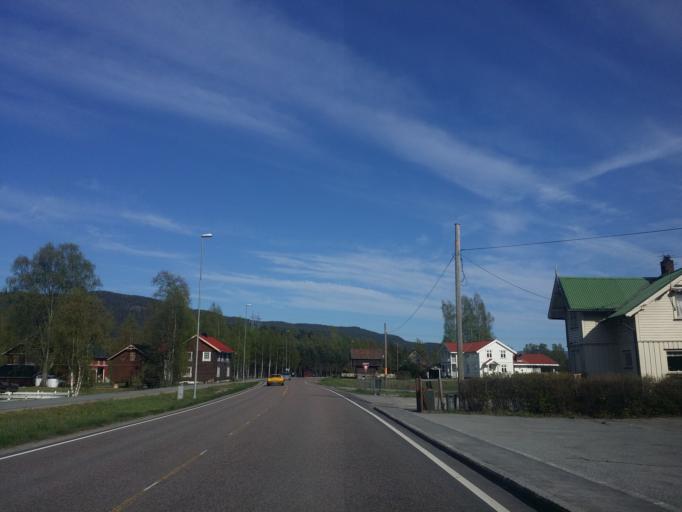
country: NO
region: Telemark
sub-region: Notodden
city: Notodden
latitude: 59.5963
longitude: 9.1363
